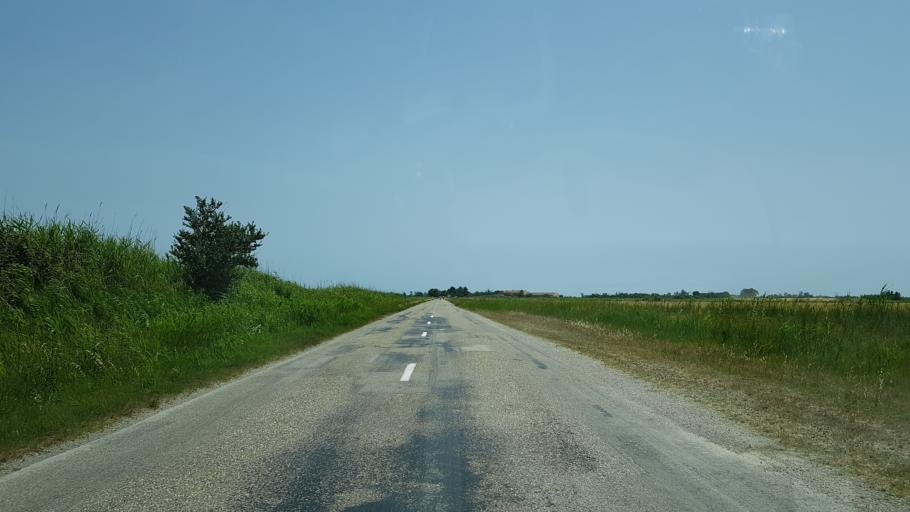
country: FR
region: Provence-Alpes-Cote d'Azur
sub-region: Departement des Bouches-du-Rhone
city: Port-Saint-Louis-du-Rhone
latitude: 43.4366
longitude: 4.6828
